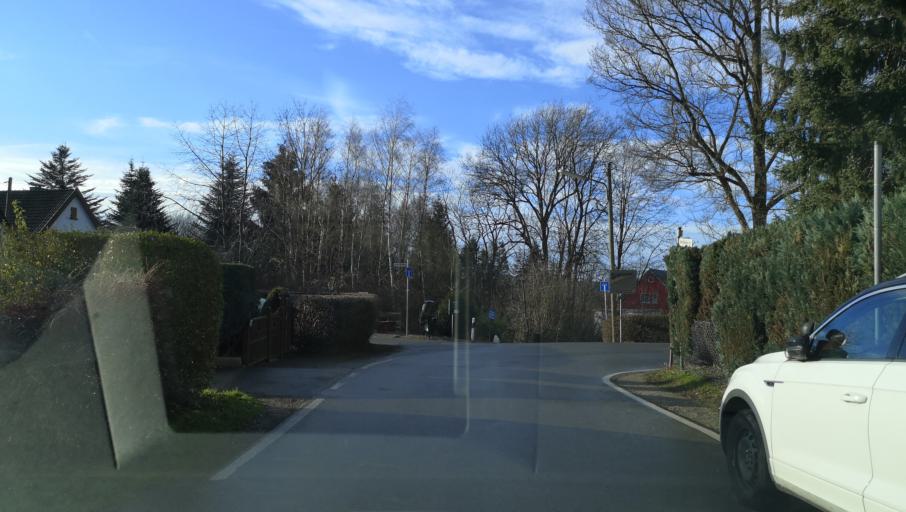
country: DE
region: North Rhine-Westphalia
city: Radevormwald
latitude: 51.1903
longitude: 7.3137
